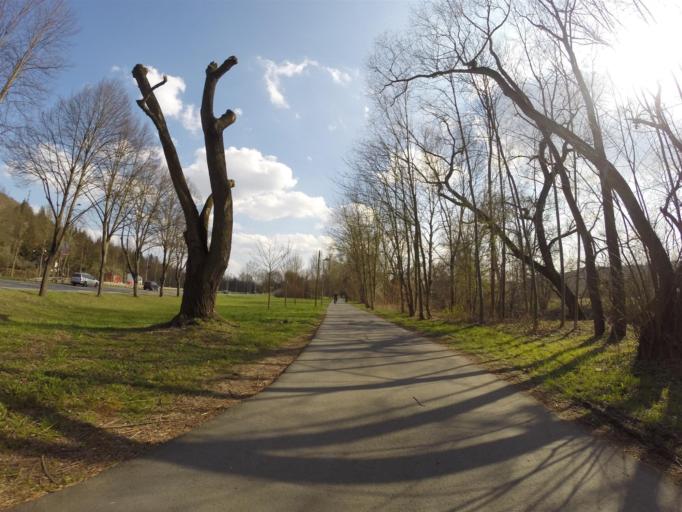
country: DE
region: Thuringia
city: Jena
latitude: 50.9011
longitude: 11.5990
